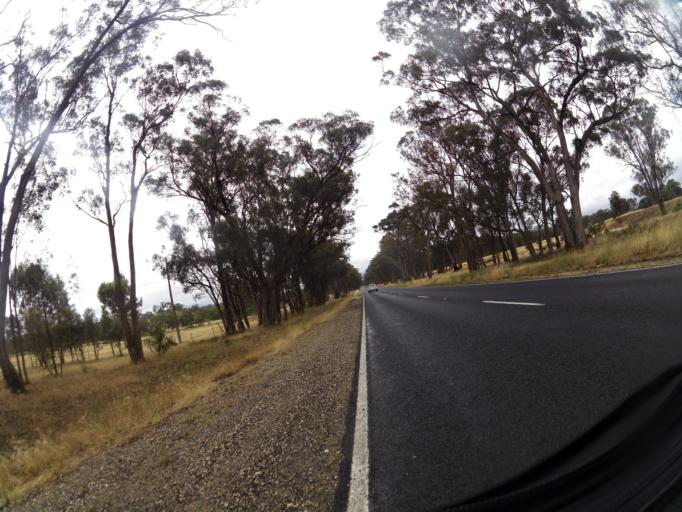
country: AU
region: Victoria
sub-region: Mount Alexander
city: Castlemaine
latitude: -37.0885
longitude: 144.1479
